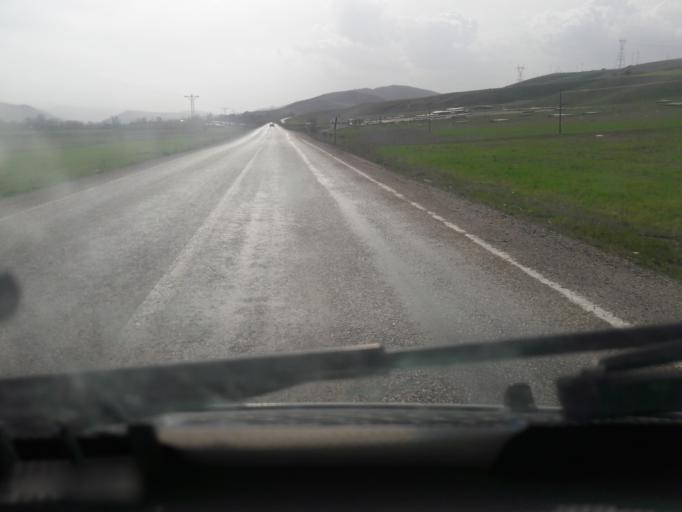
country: TR
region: Gumushane
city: Kelkit
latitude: 40.1432
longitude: 39.4088
